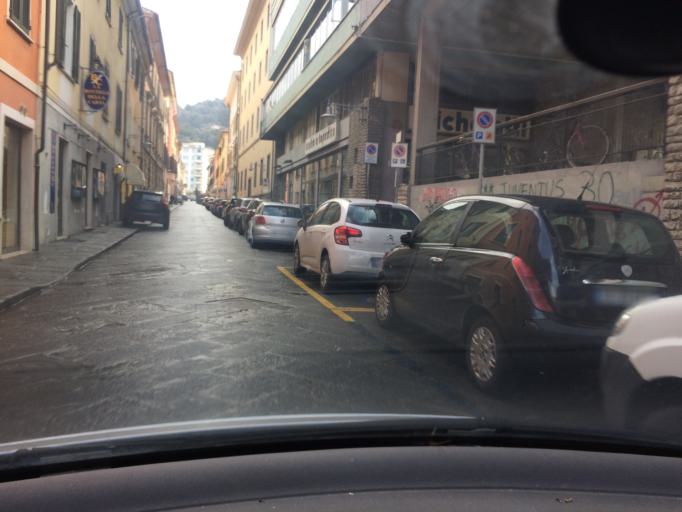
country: IT
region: Tuscany
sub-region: Provincia di Massa-Carrara
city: Massa
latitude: 44.0371
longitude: 10.1411
